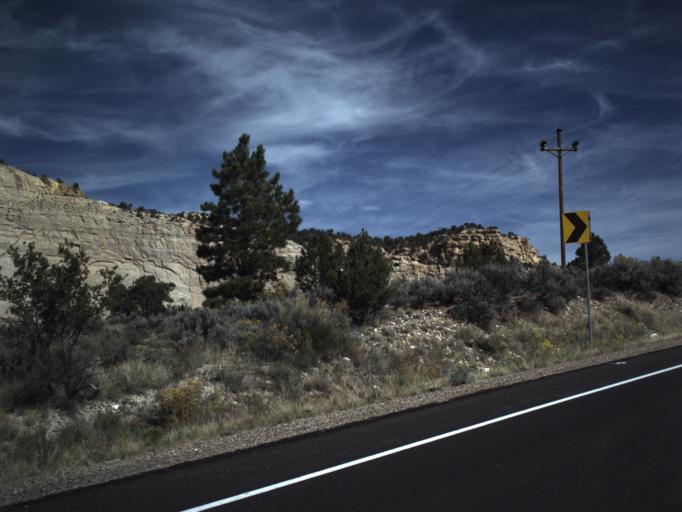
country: US
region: Utah
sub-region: Garfield County
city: Panguitch
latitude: 37.6160
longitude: -111.8945
